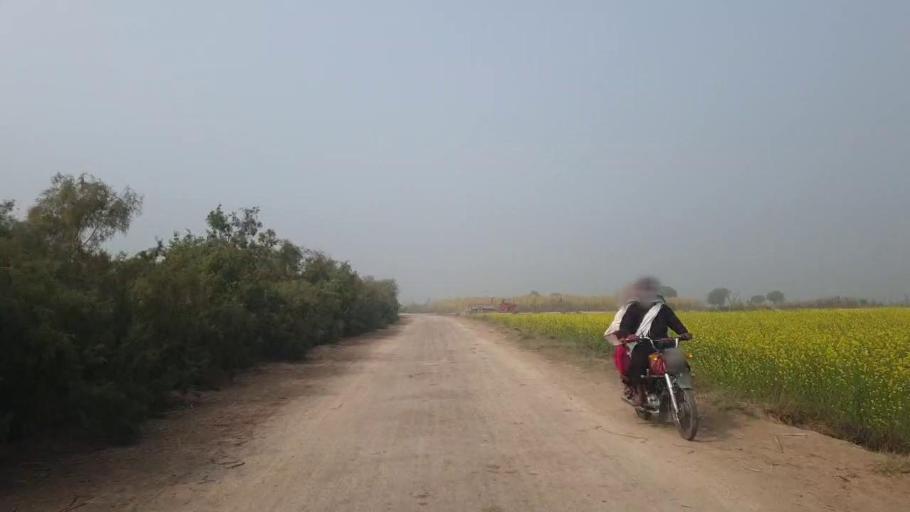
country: PK
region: Sindh
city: Bhit Shah
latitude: 25.8166
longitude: 68.5725
